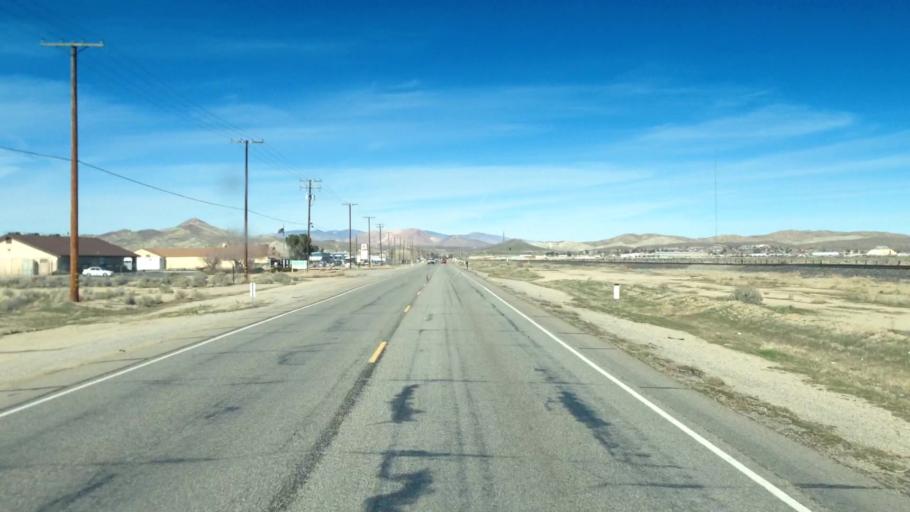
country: US
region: California
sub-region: Kern County
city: Rosamond
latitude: 34.8393
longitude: -118.1590
